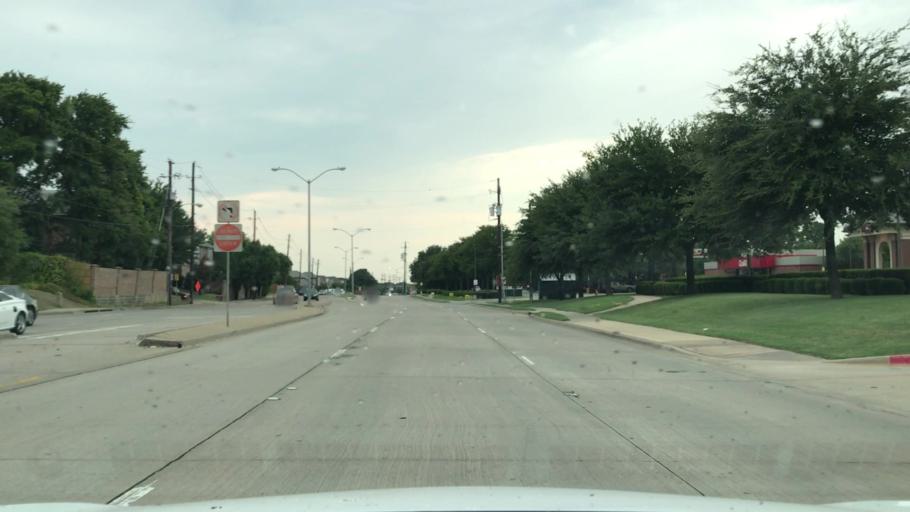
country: US
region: Texas
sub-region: Dallas County
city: Addison
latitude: 32.9971
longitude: -96.8611
